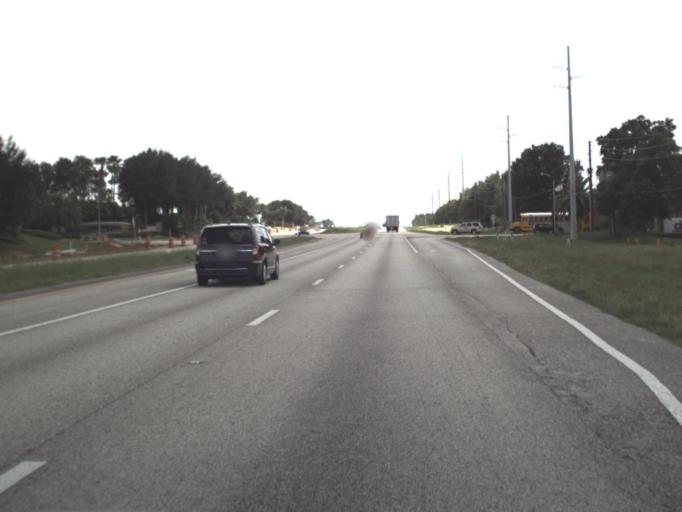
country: US
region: Florida
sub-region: Lake County
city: Four Corners
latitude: 28.2935
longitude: -81.6650
